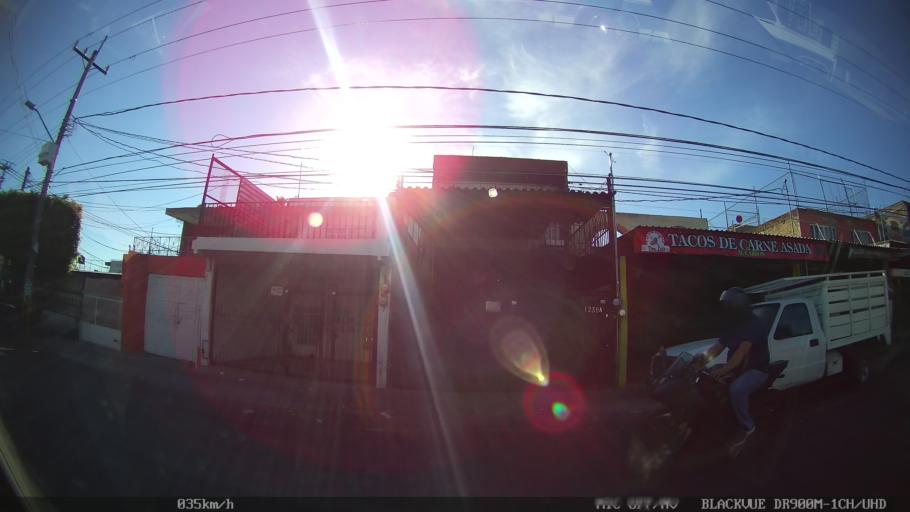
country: MX
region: Jalisco
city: Tlaquepaque
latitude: 20.6900
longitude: -103.2944
